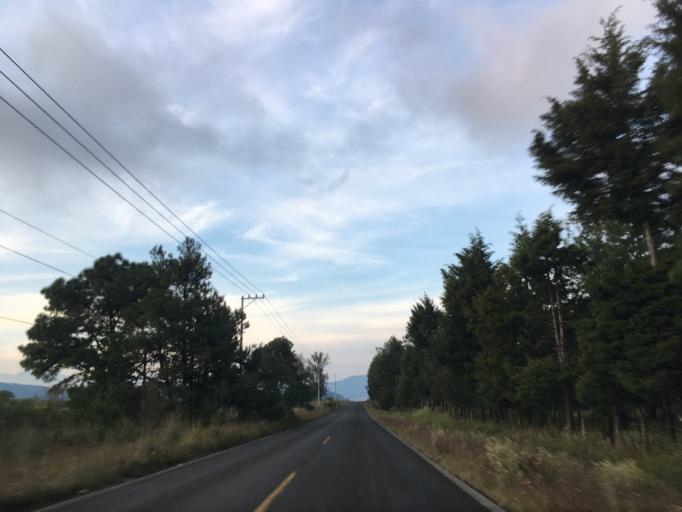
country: MX
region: Michoacan
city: Angahuan
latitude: 19.5854
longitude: -102.2369
